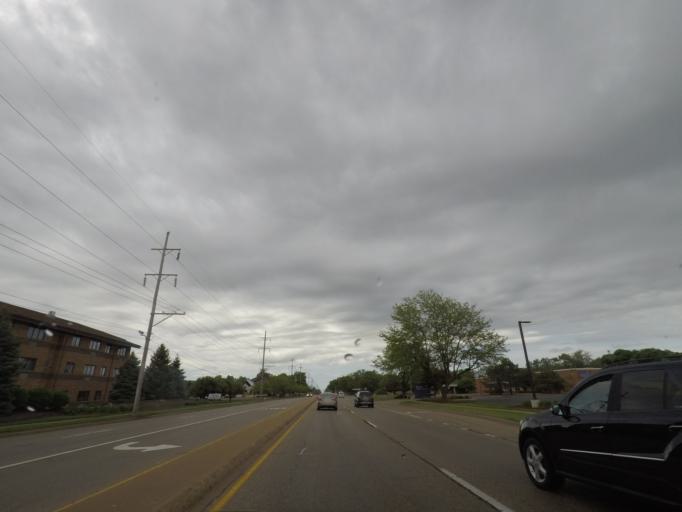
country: US
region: Illinois
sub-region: Winnebago County
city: Loves Park
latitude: 42.2813
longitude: -89.0290
